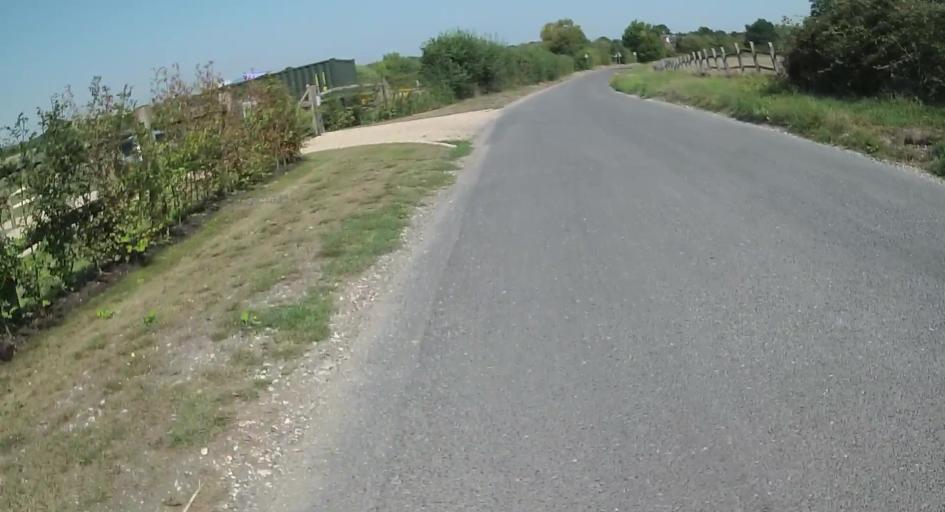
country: GB
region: England
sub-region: Hampshire
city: Kingsley
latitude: 51.1794
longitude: -0.8799
